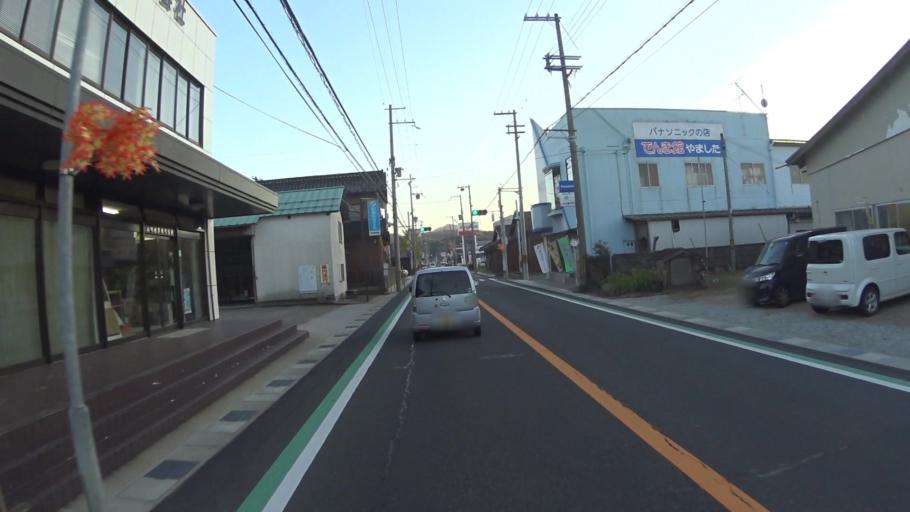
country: JP
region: Kyoto
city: Miyazu
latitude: 35.6755
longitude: 135.0282
